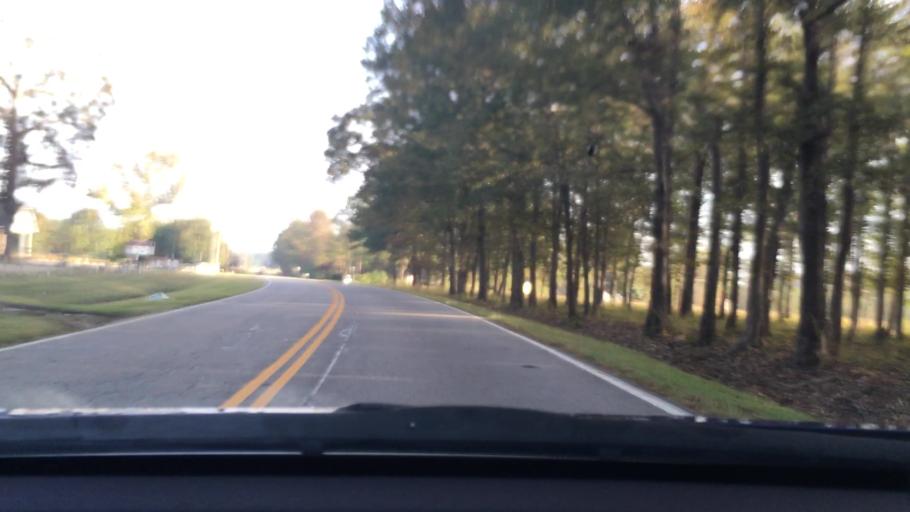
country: US
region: South Carolina
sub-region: Sumter County
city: East Sumter
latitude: 33.9969
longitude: -80.2894
